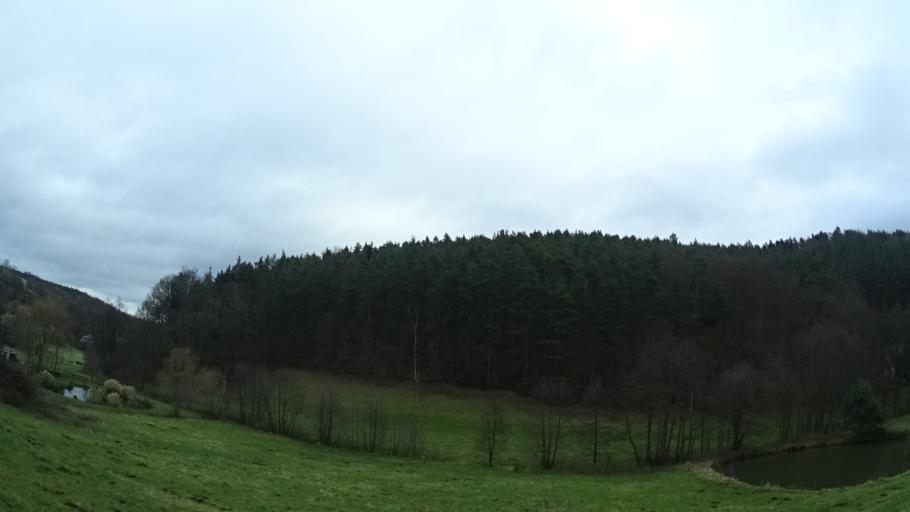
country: DE
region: Thuringia
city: Herschdorf
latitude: 50.7158
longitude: 11.4983
